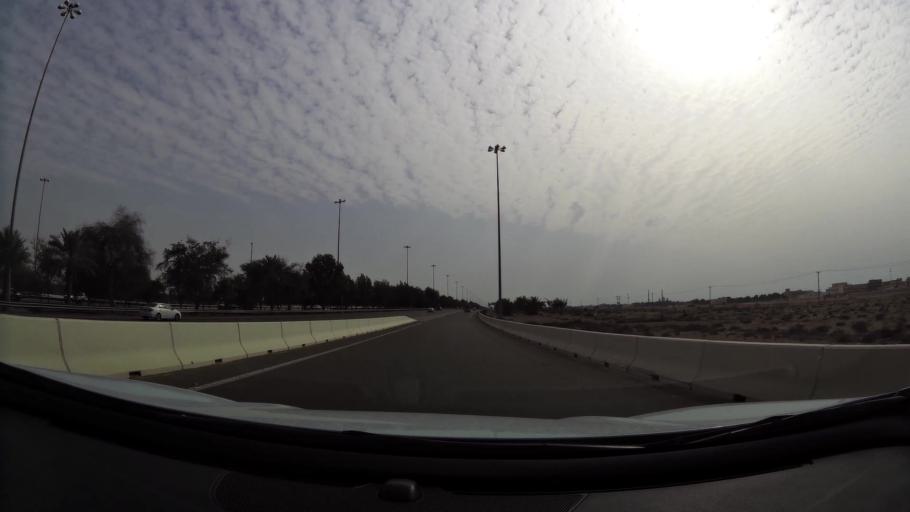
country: AE
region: Abu Dhabi
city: Abu Dhabi
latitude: 24.6193
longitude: 54.7158
